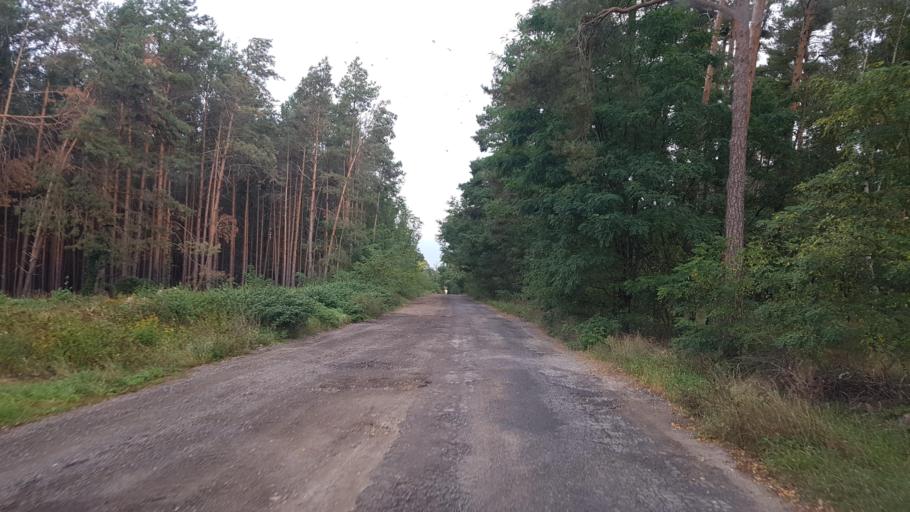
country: DE
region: Brandenburg
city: Kasel-Golzig
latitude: 51.9360
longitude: 13.7449
